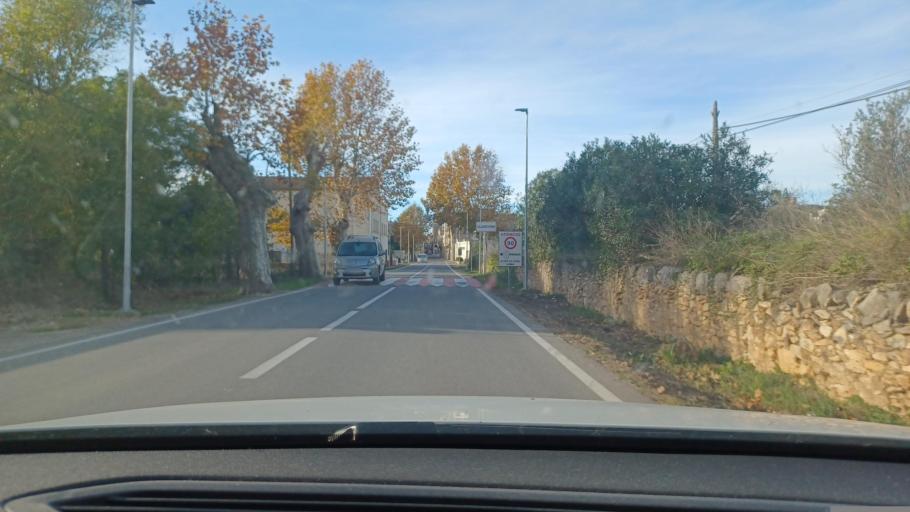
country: ES
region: Catalonia
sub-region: Provincia de Tarragona
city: Ulldecona
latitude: 40.6005
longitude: 0.4512
